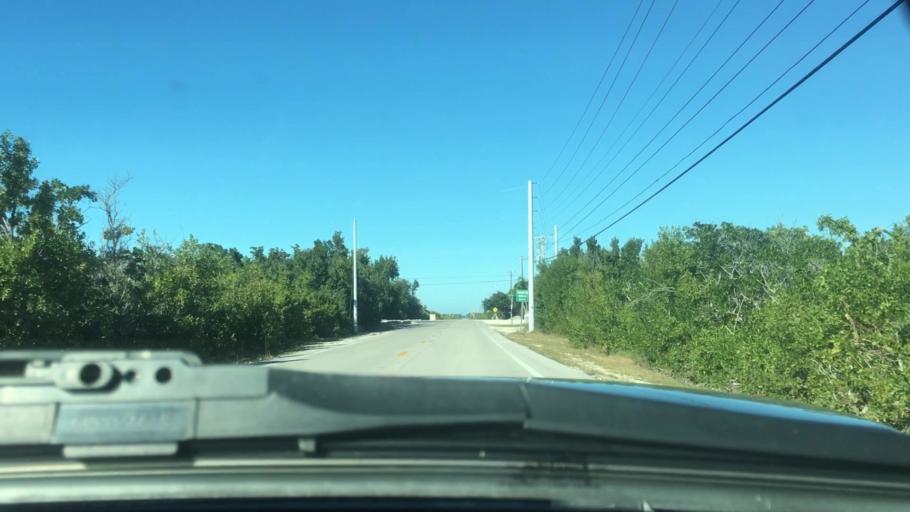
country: US
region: Florida
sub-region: Monroe County
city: Cudjoe Key
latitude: 24.6765
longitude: -81.4996
